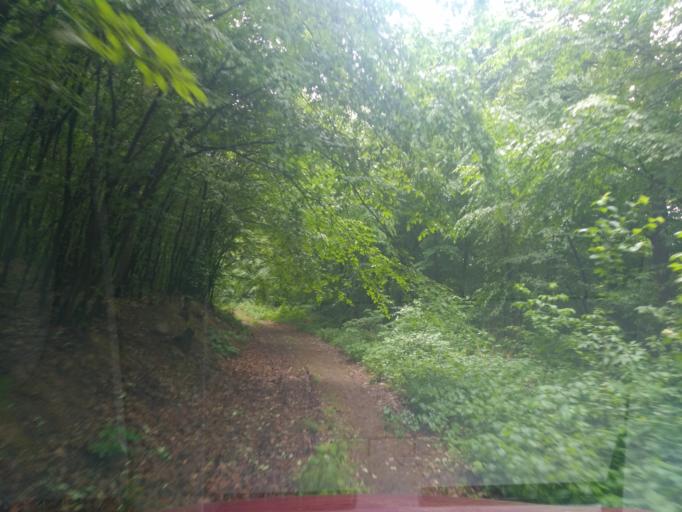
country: SK
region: Kosicky
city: Moldava nad Bodvou
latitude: 48.6962
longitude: 21.0728
